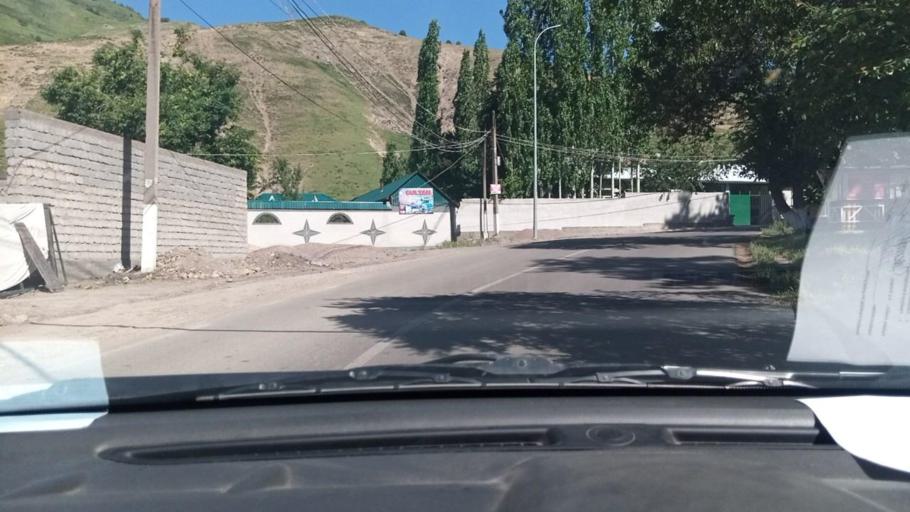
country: UZ
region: Toshkent
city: Yangiobod
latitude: 41.1167
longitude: 70.0906
